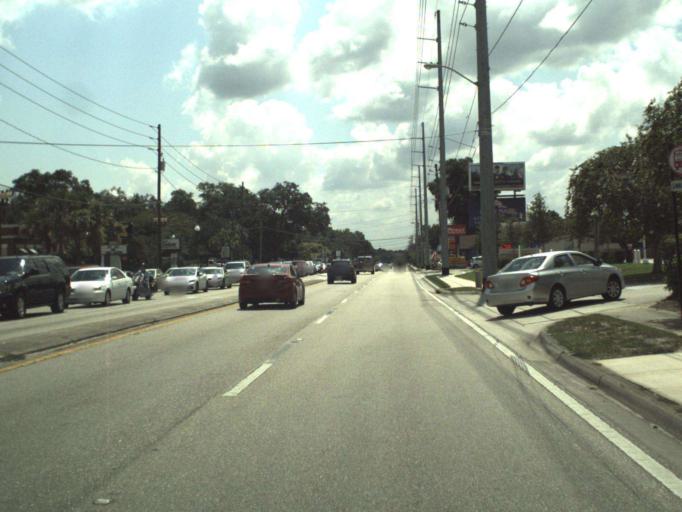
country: US
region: Florida
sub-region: Seminole County
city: Longwood
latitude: 28.6978
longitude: -81.3458
